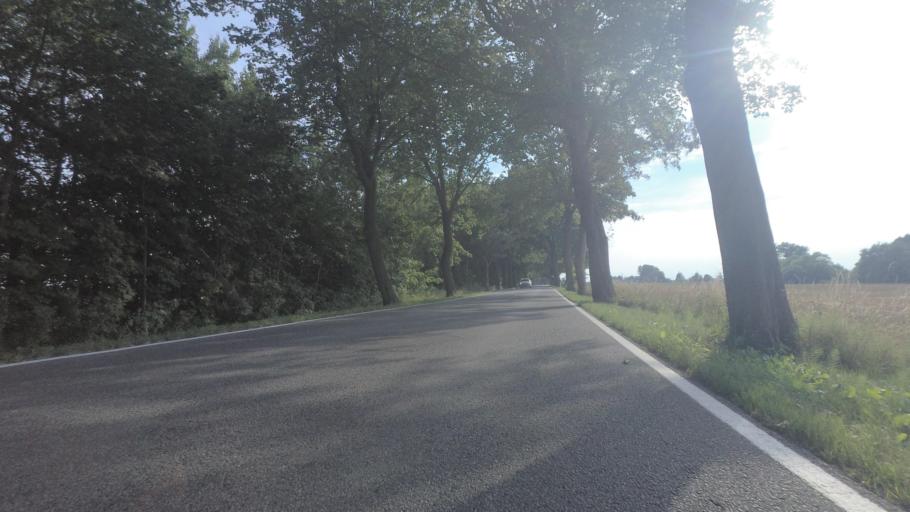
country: DE
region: Mecklenburg-Vorpommern
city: Demmin
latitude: 53.9233
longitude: 13.0754
